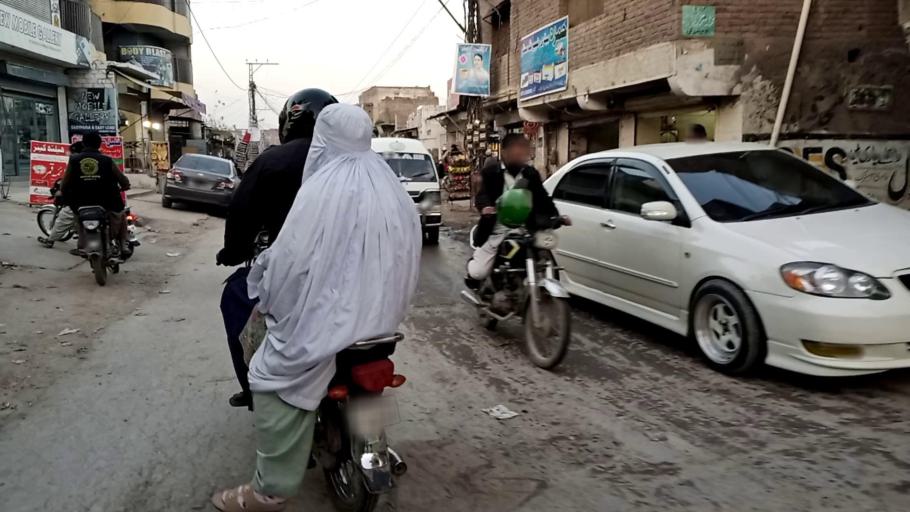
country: PK
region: Khyber Pakhtunkhwa
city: Peshawar
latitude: 34.0262
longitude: 71.4875
